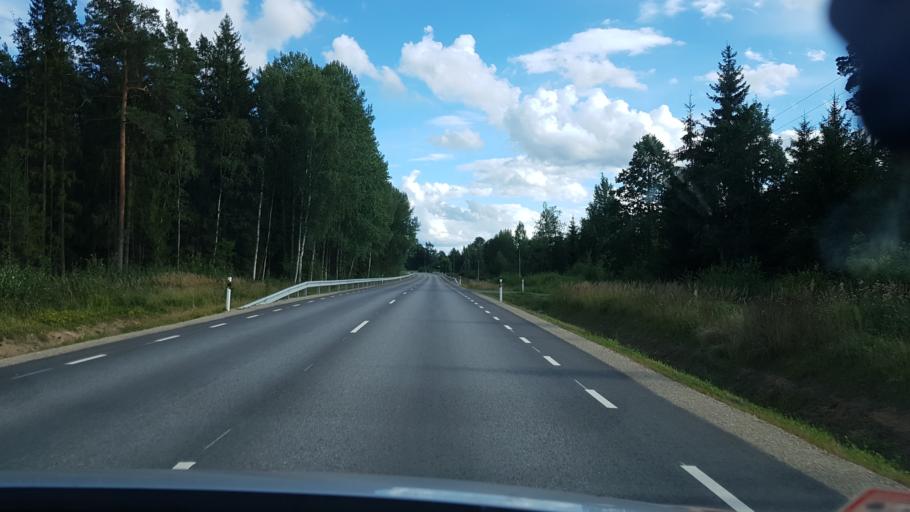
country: EE
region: Polvamaa
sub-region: Polva linn
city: Polva
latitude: 58.0854
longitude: 27.2354
